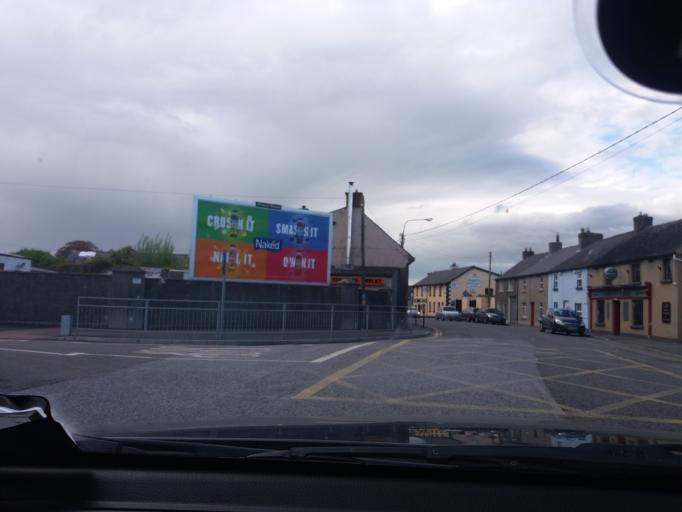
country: IE
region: Leinster
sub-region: Kilkenny
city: Kilkenny
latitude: 52.6455
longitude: -7.2501
